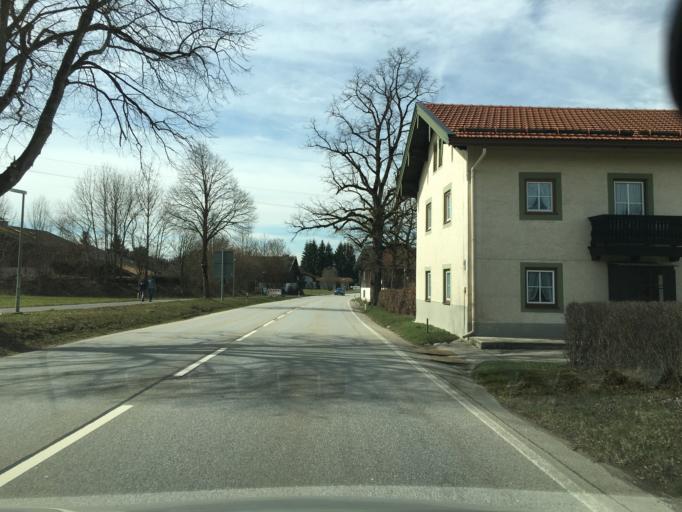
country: DE
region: Bavaria
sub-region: Upper Bavaria
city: Siegsdorf
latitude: 47.8192
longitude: 12.6639
